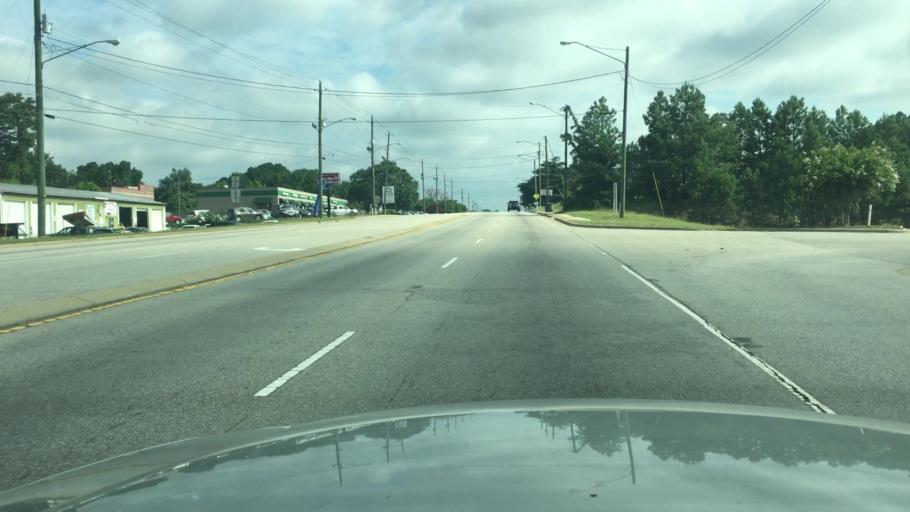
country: US
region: North Carolina
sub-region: Cumberland County
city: Hope Mills
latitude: 34.9963
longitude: -78.9675
